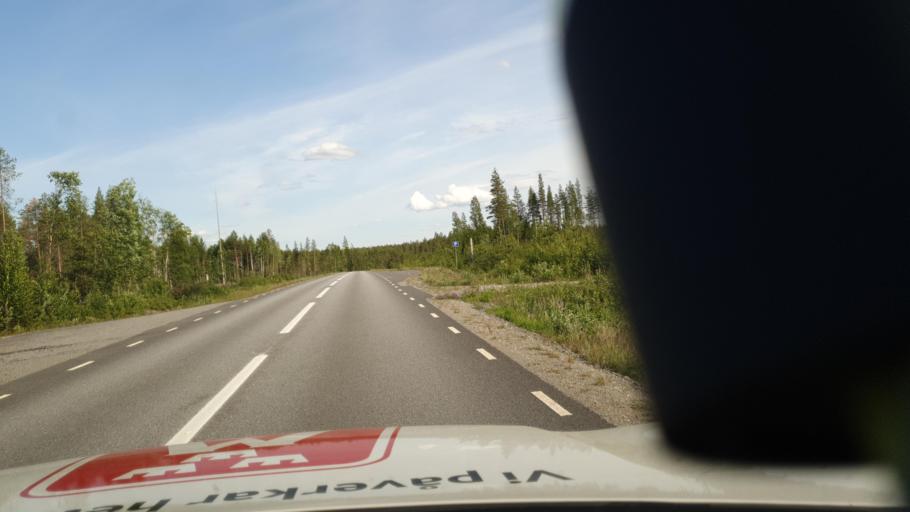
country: SE
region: Vaesterbotten
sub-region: Skelleftea Kommun
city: Forsbacka
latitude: 64.7336
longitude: 20.3850
